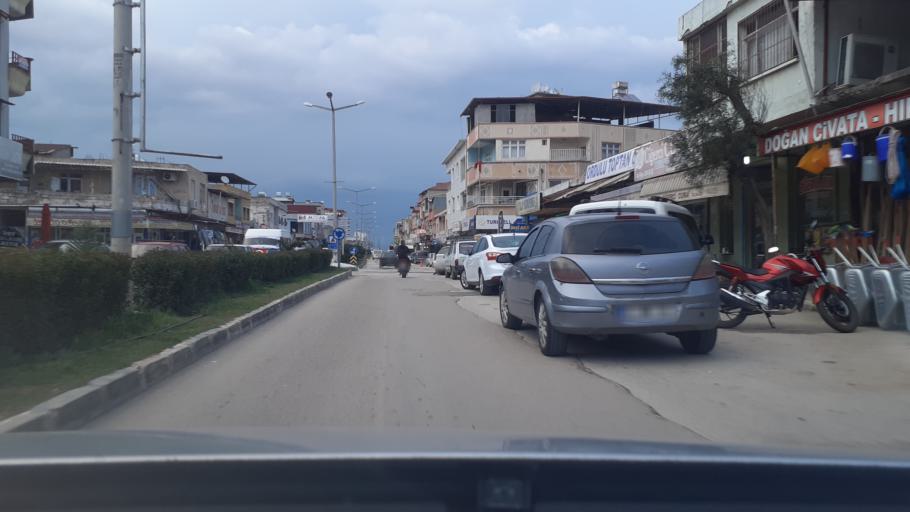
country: TR
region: Hatay
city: Kirikhan
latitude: 36.4963
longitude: 36.3605
